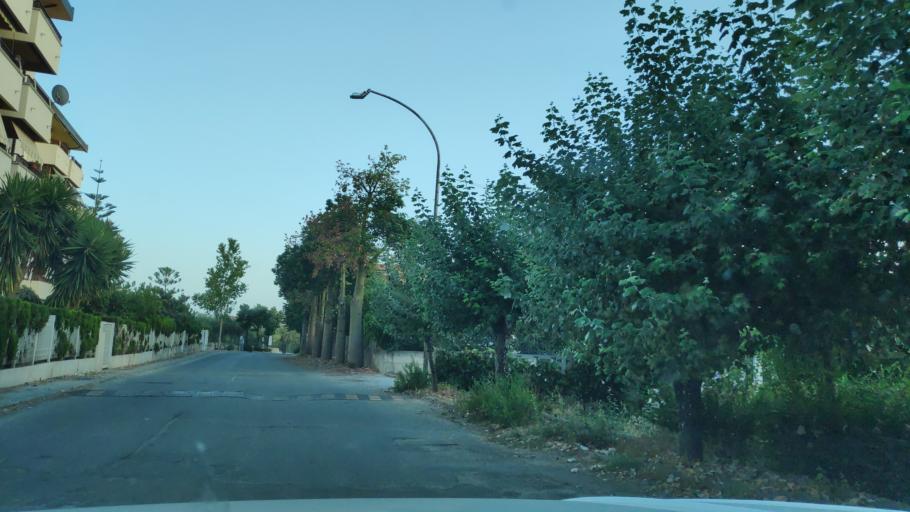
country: IT
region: Calabria
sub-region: Provincia di Reggio Calabria
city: Bova Marina
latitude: 37.9310
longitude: 15.9109
